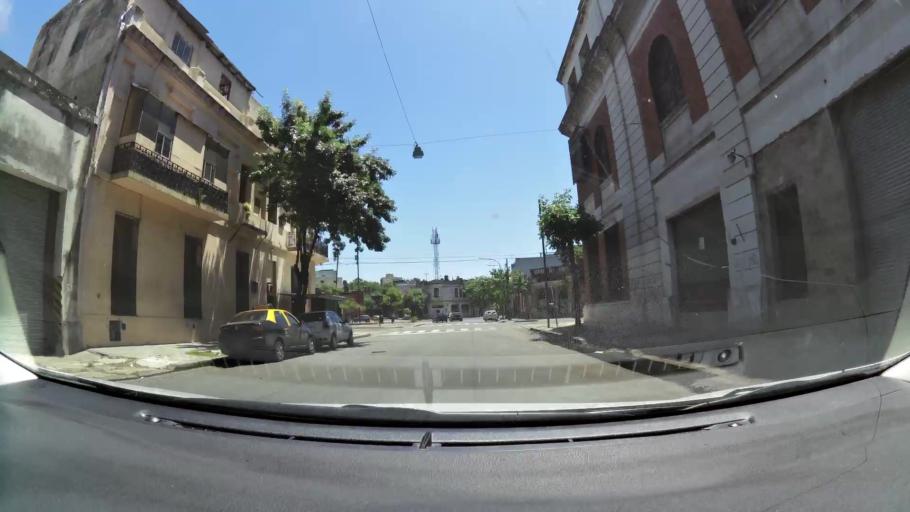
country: AR
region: Buenos Aires F.D.
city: Buenos Aires
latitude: -34.6398
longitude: -58.3881
